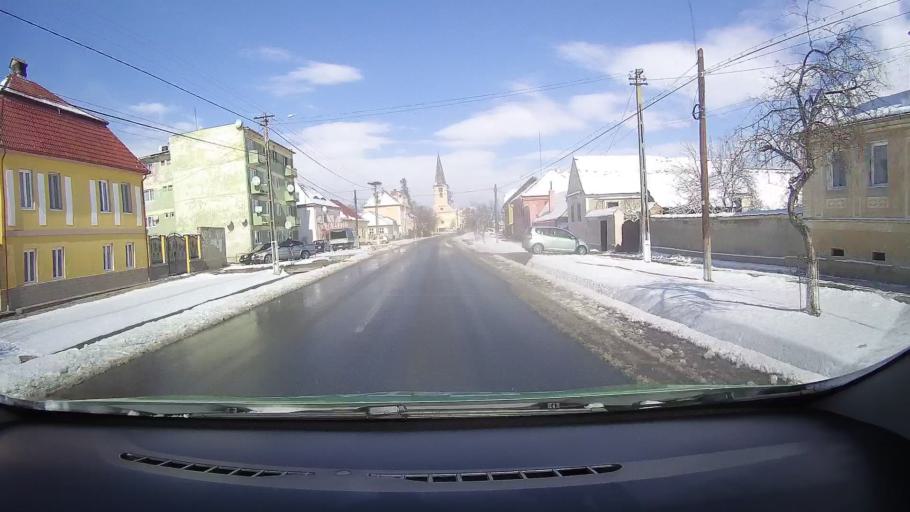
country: RO
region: Sibiu
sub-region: Comuna Nocrich
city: Nocrich
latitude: 45.8934
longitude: 24.4540
